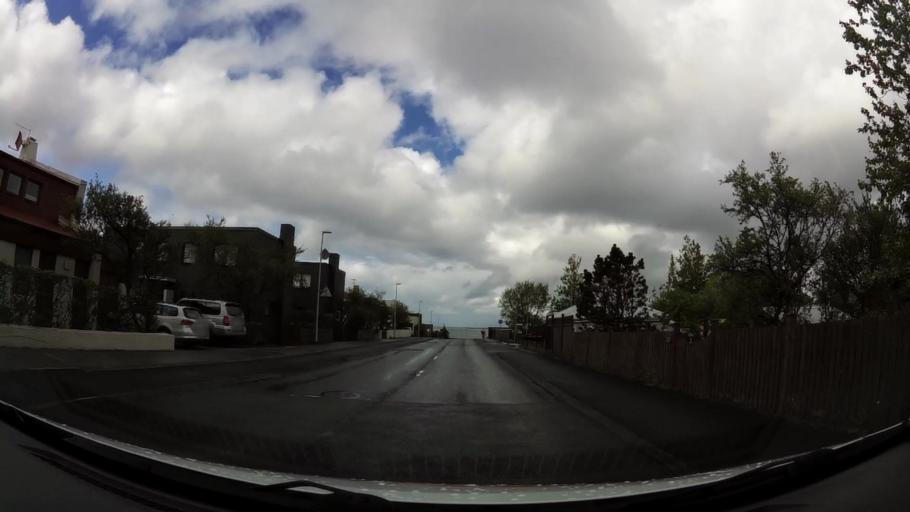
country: IS
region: Capital Region
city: Kopavogur
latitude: 64.1308
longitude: -21.9543
